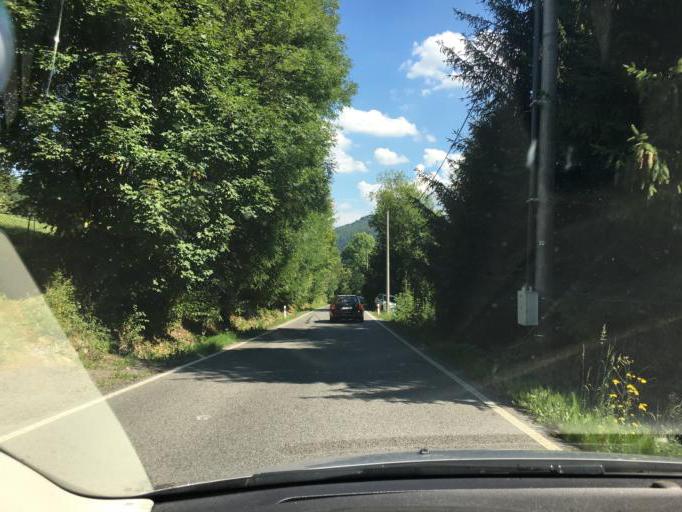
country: CZ
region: Liberecky
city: Mala Skala
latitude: 50.6450
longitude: 15.1750
